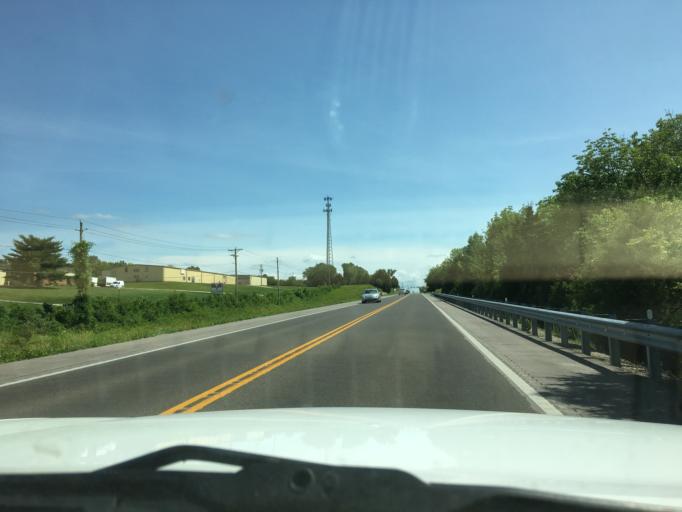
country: US
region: Missouri
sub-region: Franklin County
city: Union
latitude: 38.4874
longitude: -91.0053
